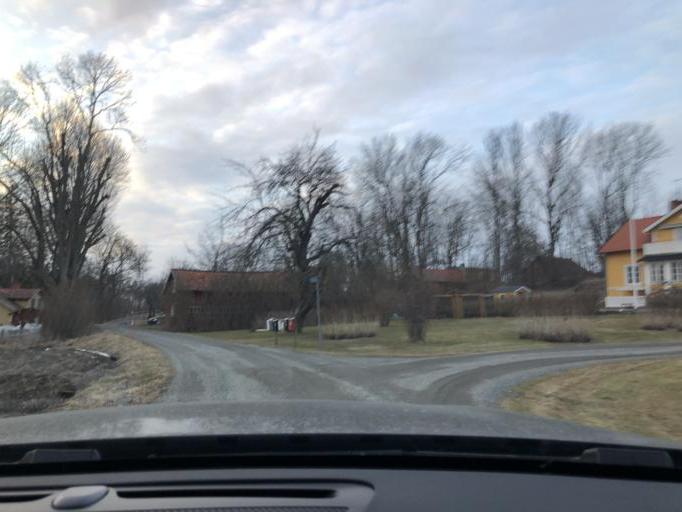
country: SE
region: Uppsala
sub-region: Uppsala Kommun
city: Gamla Uppsala
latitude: 59.9211
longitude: 17.6304
